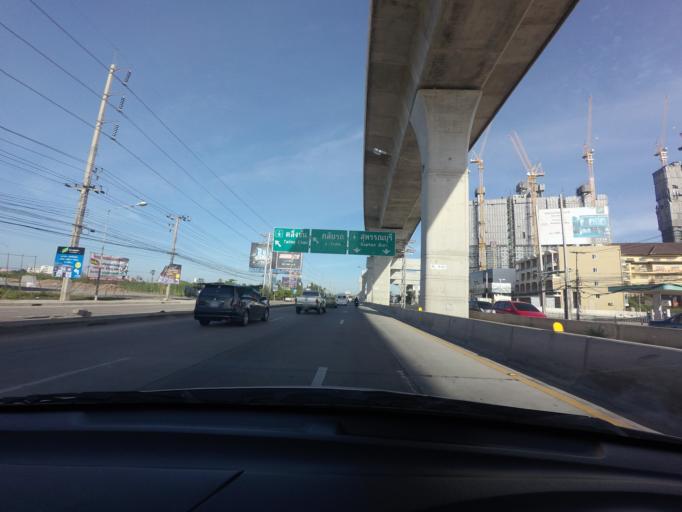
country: TH
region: Nonthaburi
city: Bang Bua Thong
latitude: 13.8744
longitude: 100.4156
